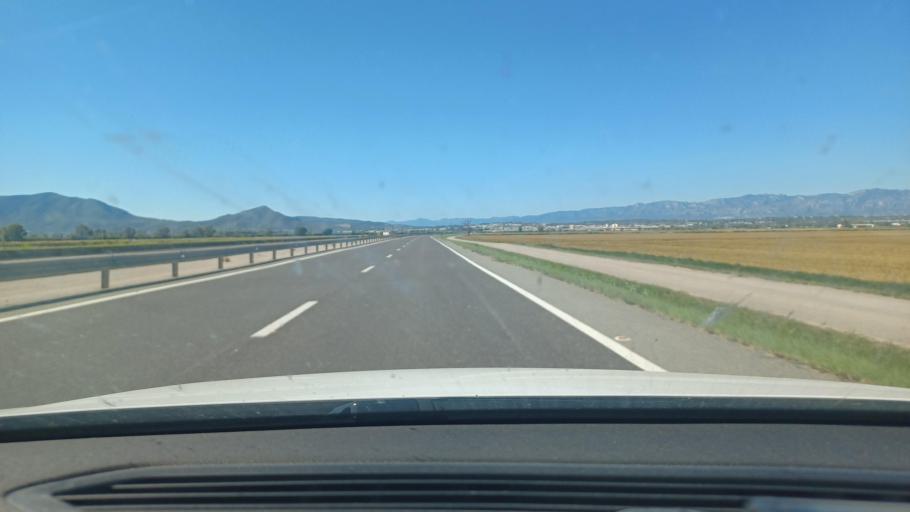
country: ES
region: Catalonia
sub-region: Provincia de Tarragona
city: Amposta
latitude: 40.7135
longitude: 0.6209
